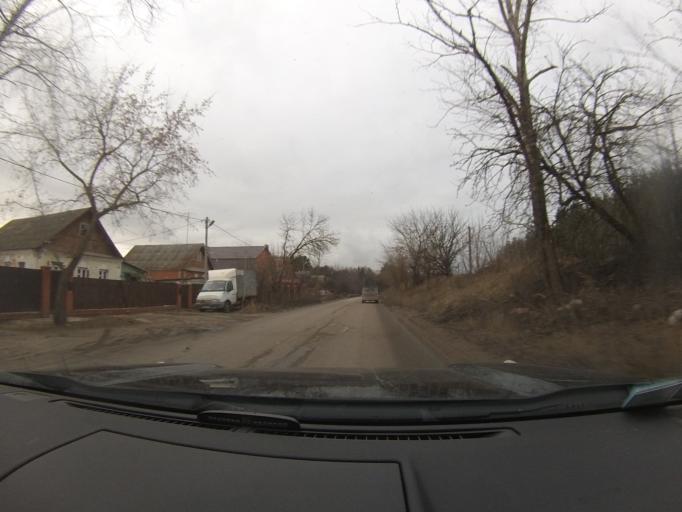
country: RU
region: Moskovskaya
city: Voskresensk
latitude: 55.3310
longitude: 38.6786
